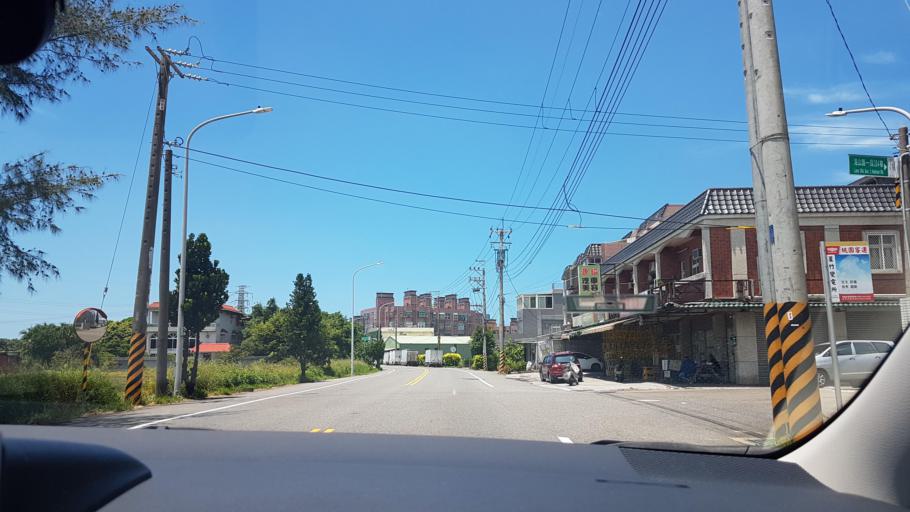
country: TW
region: Taiwan
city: Taoyuan City
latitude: 25.0978
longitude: 121.2632
